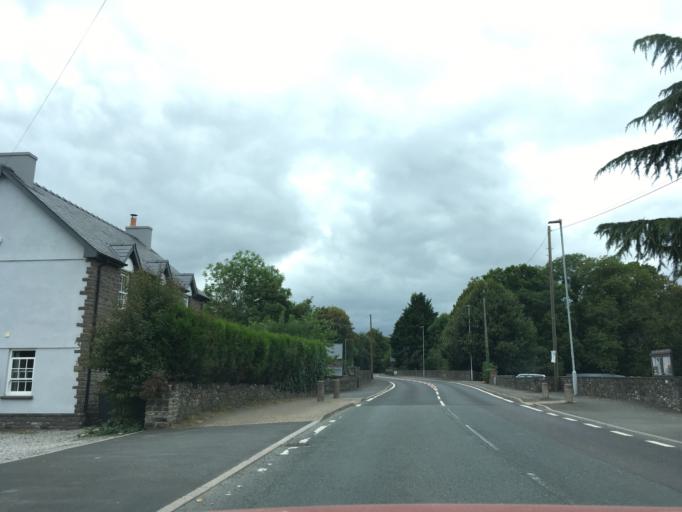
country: GB
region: Wales
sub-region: Monmouthshire
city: Gilwern
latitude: 51.8405
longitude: -3.1061
